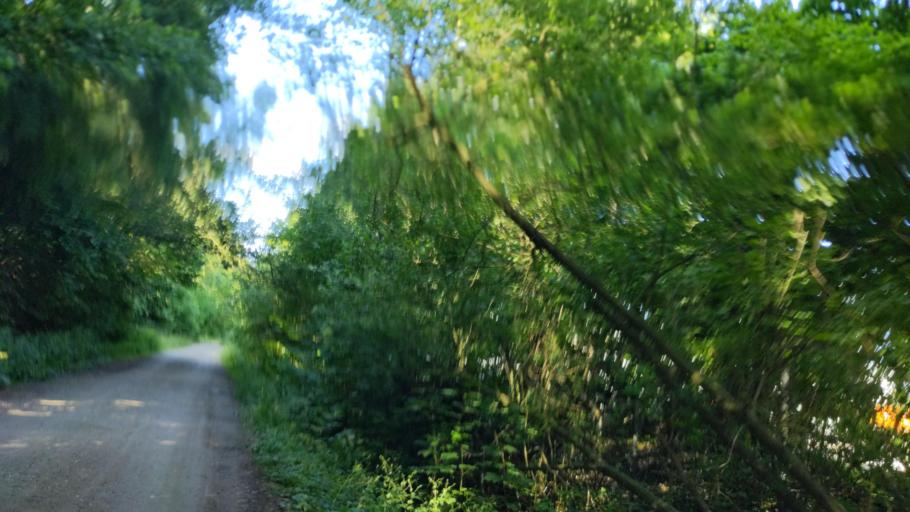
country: DE
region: Schleswig-Holstein
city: Krummesse
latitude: 53.8152
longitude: 10.6553
